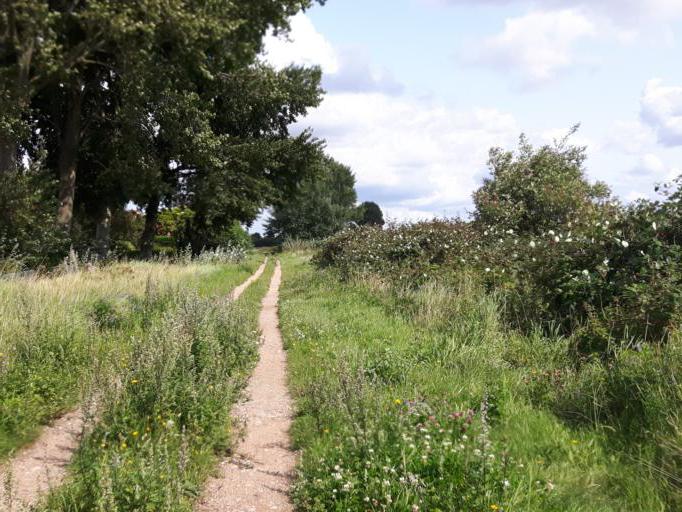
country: NL
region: Zeeland
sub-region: Gemeente Borsele
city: Borssele
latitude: 51.4670
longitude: 3.7994
